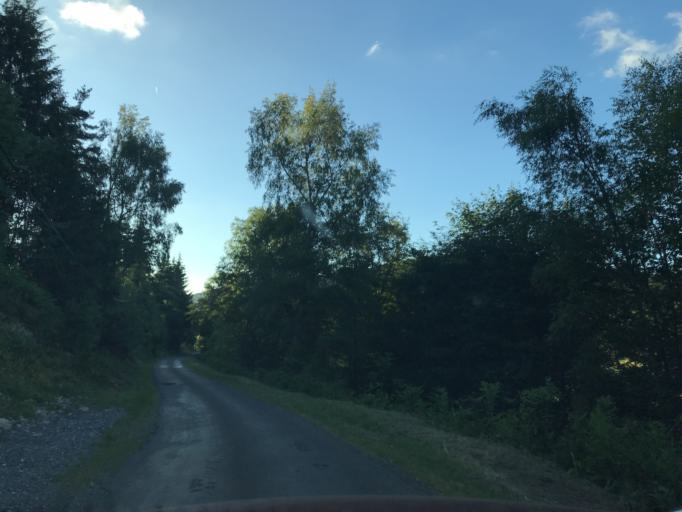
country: FR
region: Rhone-Alpes
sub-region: Departement de la Loire
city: Noiretable
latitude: 45.7828
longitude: 3.6878
